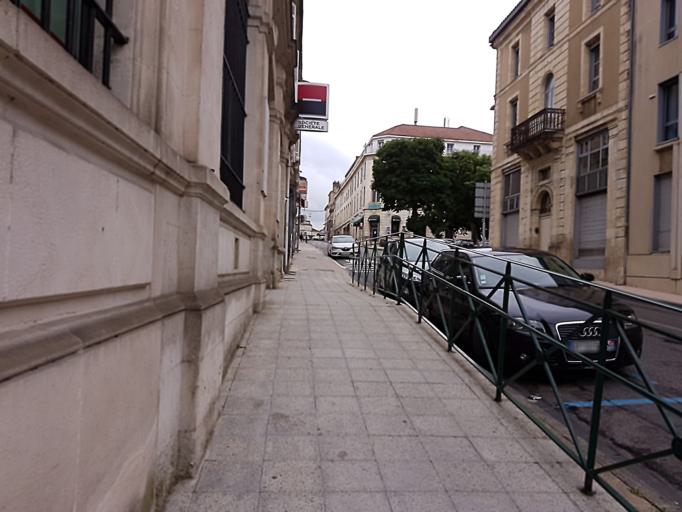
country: FR
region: Midi-Pyrenees
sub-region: Departement du Gers
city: Auch
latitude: 43.6481
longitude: 0.5860
